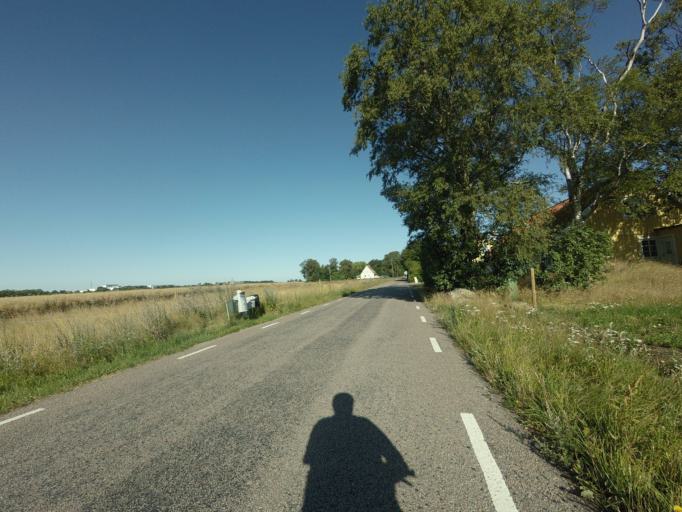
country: SE
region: Skane
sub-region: Hoganas Kommun
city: Hoganas
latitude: 56.1651
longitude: 12.5957
